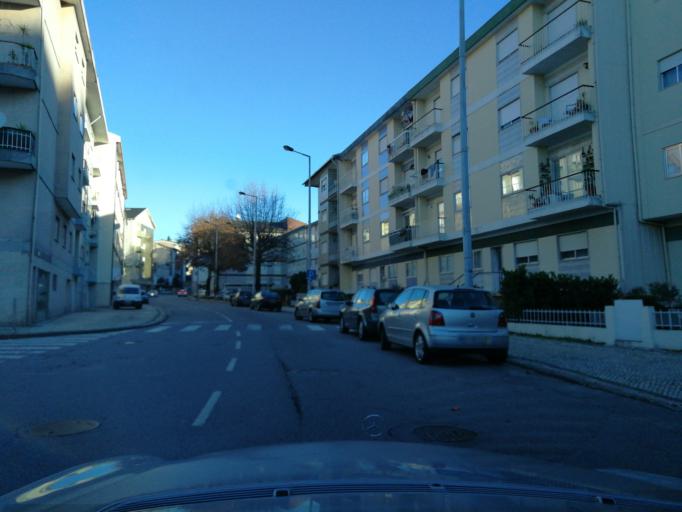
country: PT
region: Braga
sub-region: Braga
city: Braga
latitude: 41.5564
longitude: -8.4081
